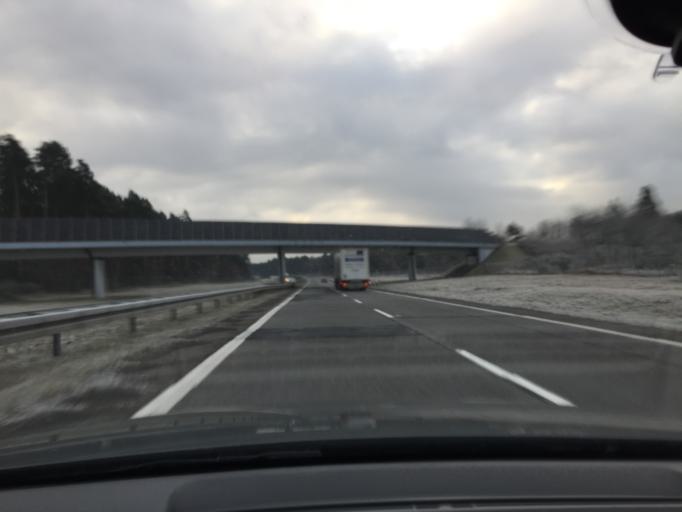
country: PL
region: Lubusz
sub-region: Powiat zarski
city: Trzebiel
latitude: 51.6316
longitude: 14.8774
